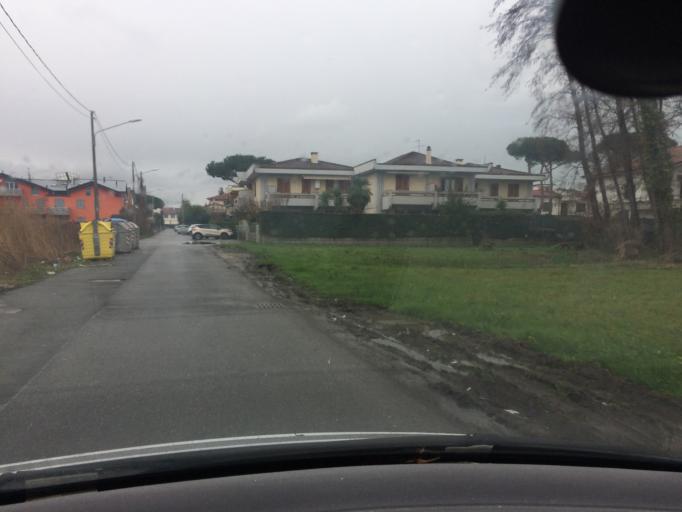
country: IT
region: Tuscany
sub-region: Provincia di Massa-Carrara
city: Massa
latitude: 44.0144
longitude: 10.1023
